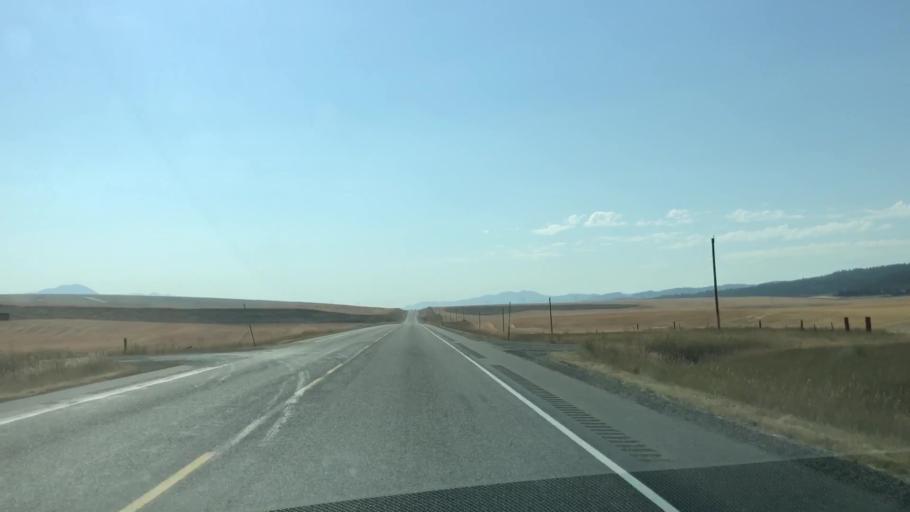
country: US
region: Idaho
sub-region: Madison County
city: Rexburg
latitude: 43.5384
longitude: -111.5145
